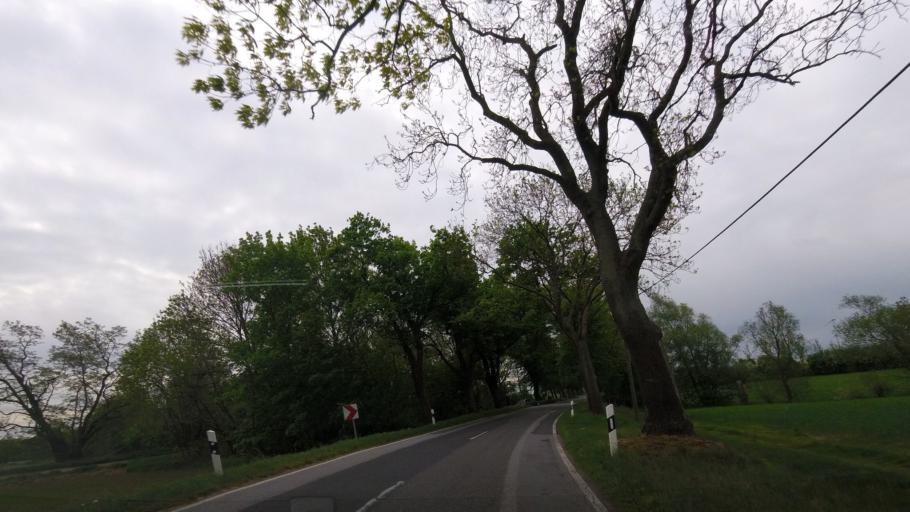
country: DE
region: Brandenburg
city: Dahme
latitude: 51.8881
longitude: 13.4183
